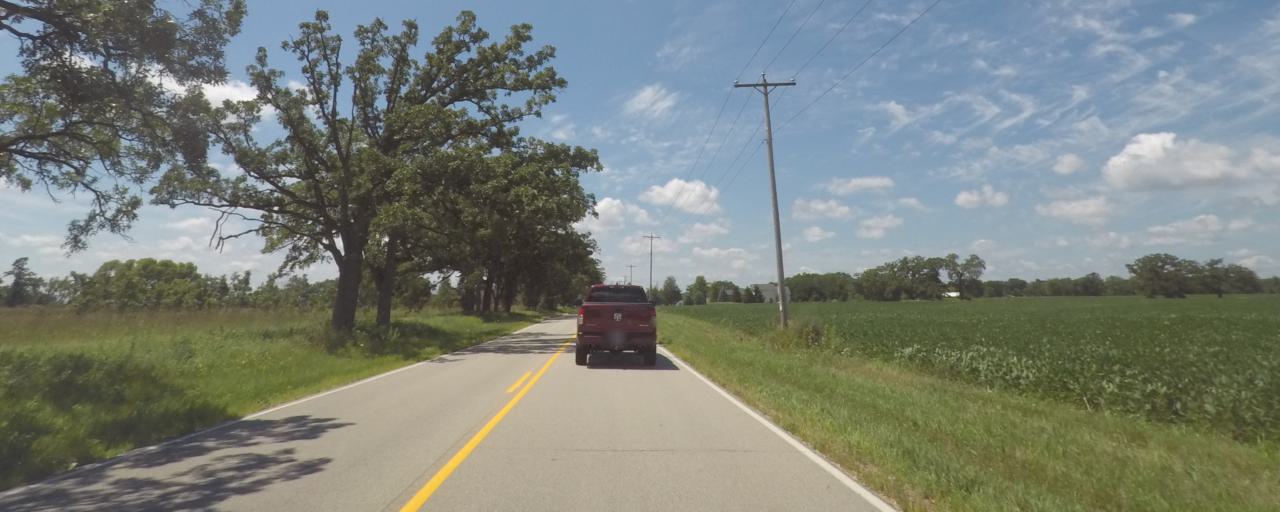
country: US
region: Wisconsin
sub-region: Waukesha County
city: Eagle
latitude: 42.9264
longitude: -88.5259
